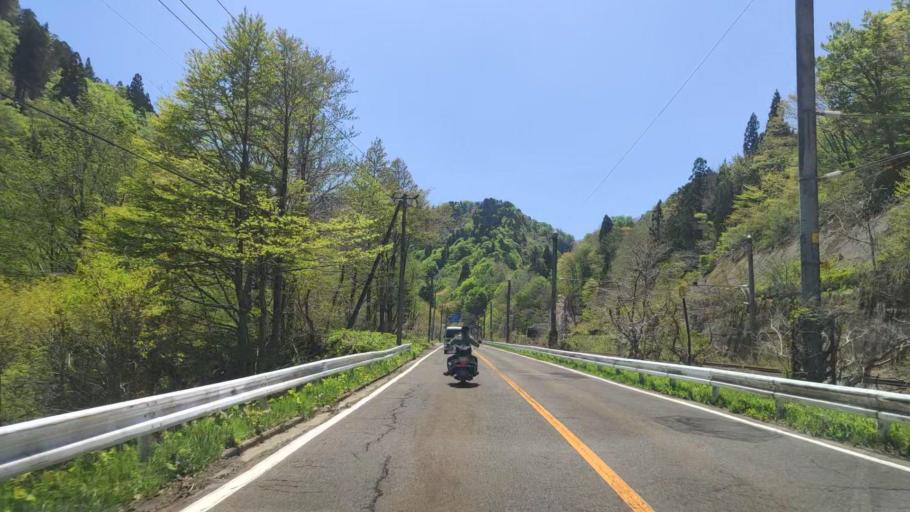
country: JP
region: Akita
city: Yuzawa
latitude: 39.0149
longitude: 140.3722
